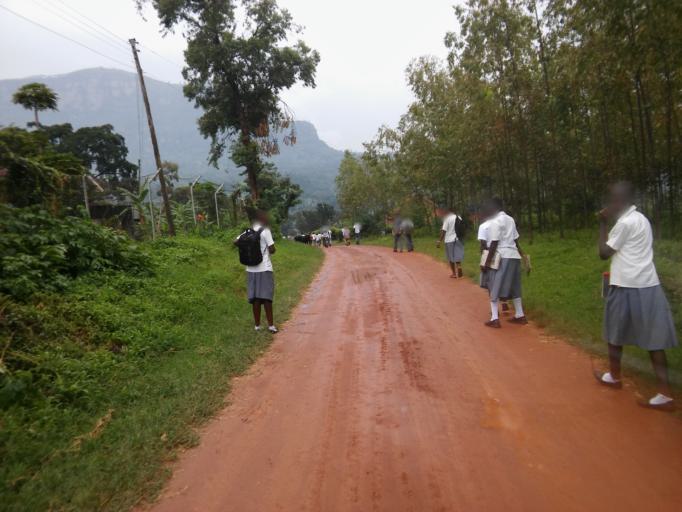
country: UG
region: Eastern Region
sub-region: Bududa District
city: Bududa
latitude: 0.9866
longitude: 34.2260
